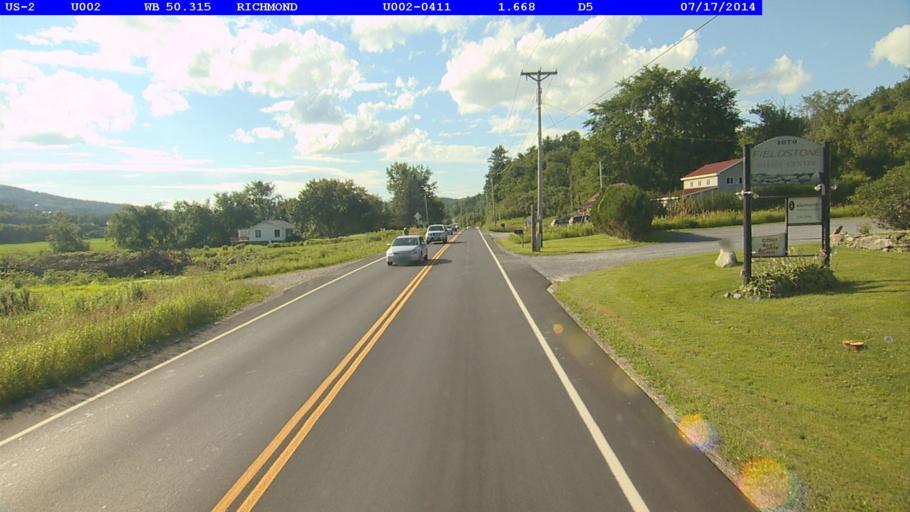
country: US
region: Vermont
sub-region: Chittenden County
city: Williston
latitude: 44.4182
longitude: -73.0008
